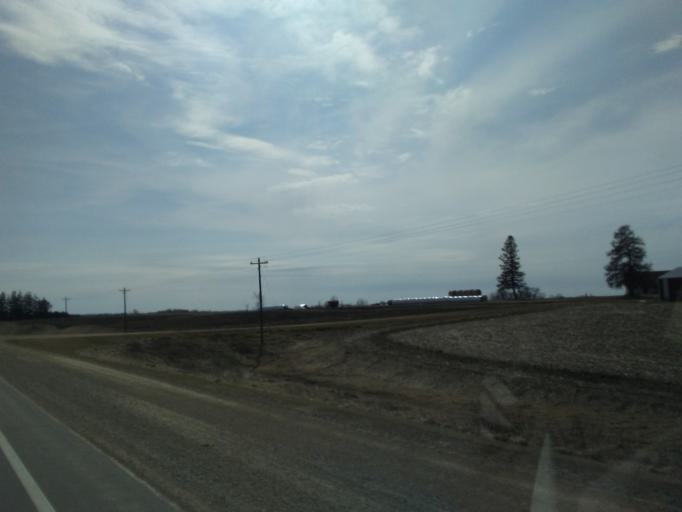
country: US
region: Iowa
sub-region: Winneshiek County
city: Decorah
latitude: 43.4380
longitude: -91.8613
